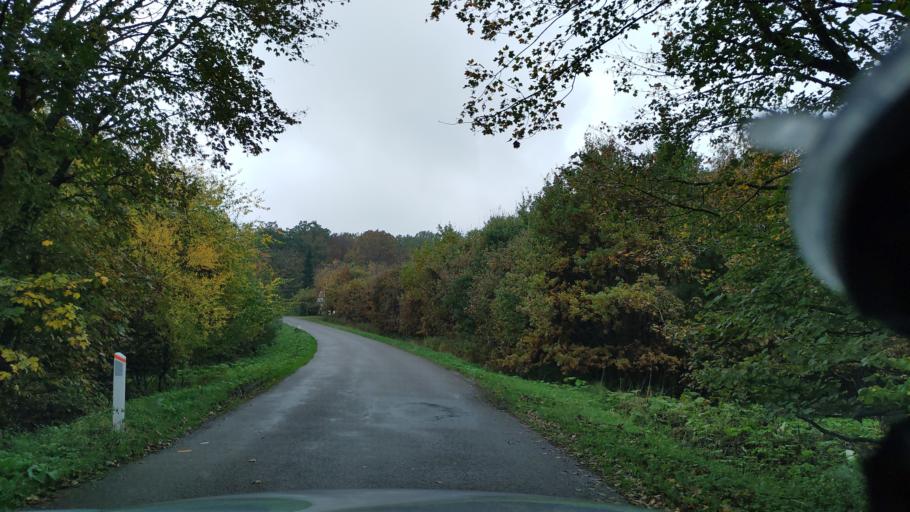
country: DK
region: Zealand
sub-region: Faxe Kommune
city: Ronnede
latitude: 55.2570
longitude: 11.9614
